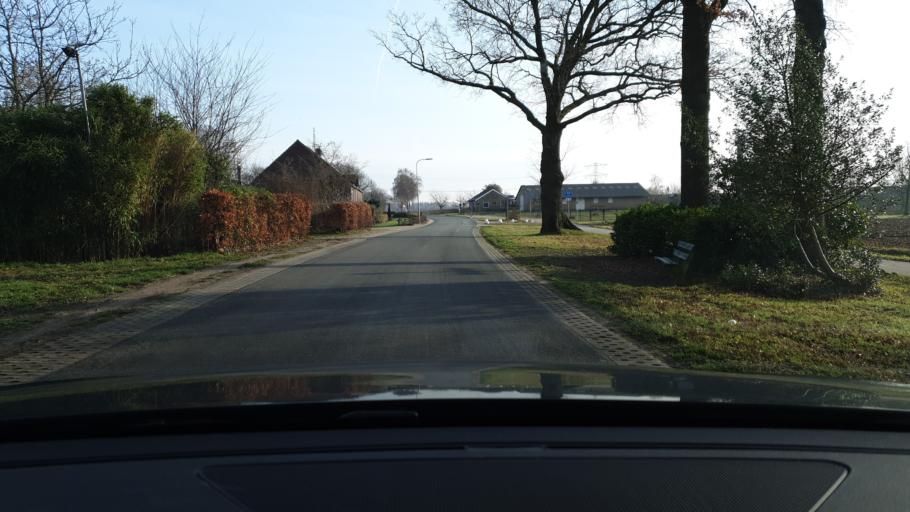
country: NL
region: Limburg
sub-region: Gemeente Peel en Maas
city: Maasbree
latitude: 51.4398
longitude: 6.0902
